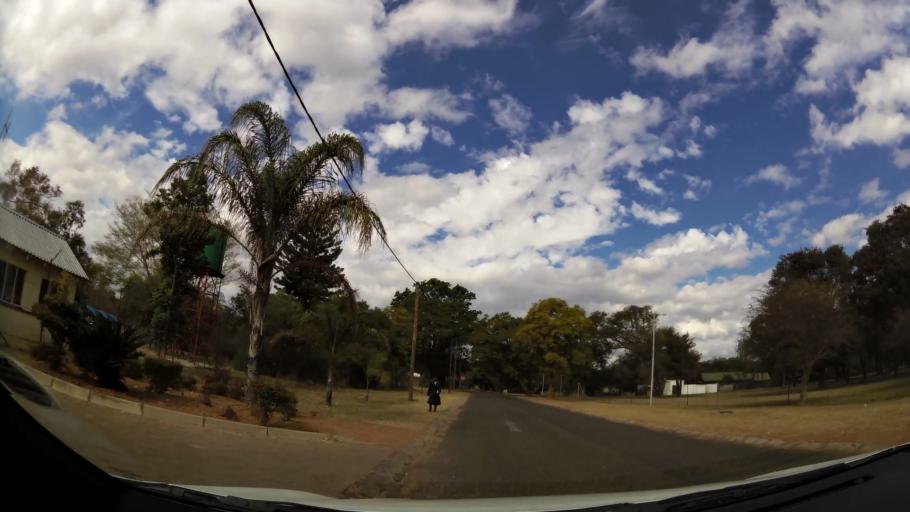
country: ZA
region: Limpopo
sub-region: Waterberg District Municipality
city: Modimolle
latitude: -24.7058
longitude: 28.4008
